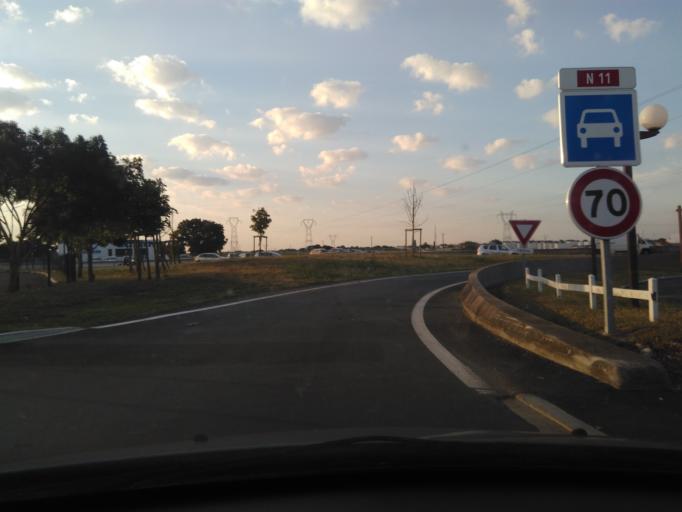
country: FR
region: Poitou-Charentes
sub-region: Departement de la Charente-Maritime
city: Puilboreau
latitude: 46.1765
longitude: -1.1077
